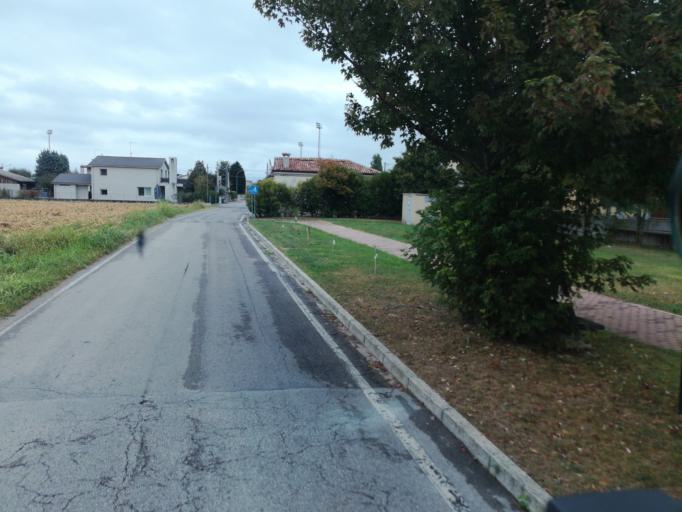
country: IT
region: Veneto
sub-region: Provincia di Vicenza
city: Rosa
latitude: 45.7274
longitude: 11.7556
